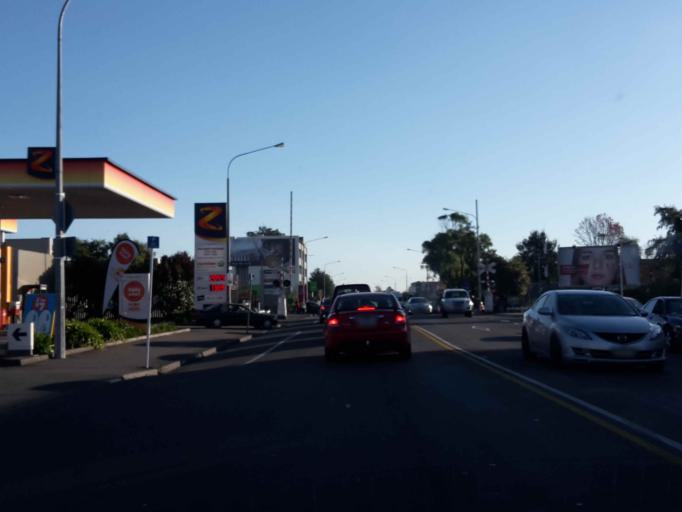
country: NZ
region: Canterbury
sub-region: Christchurch City
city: Christchurch
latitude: -43.5290
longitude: 172.6095
